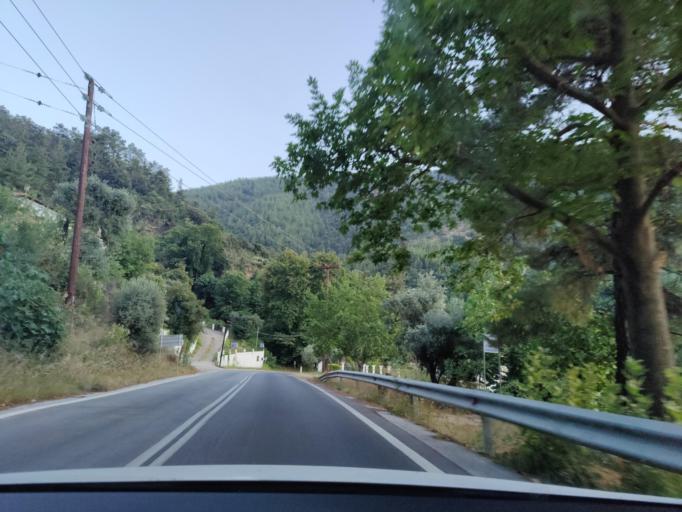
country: GR
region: East Macedonia and Thrace
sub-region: Nomos Kavalas
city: Potamia
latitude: 40.7068
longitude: 24.7634
